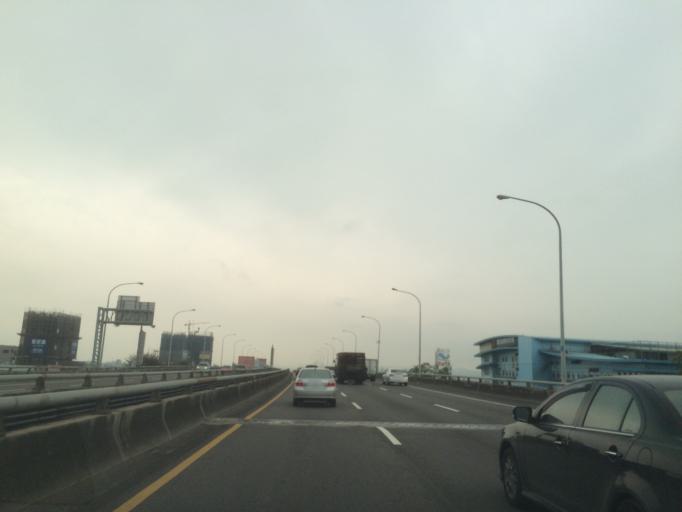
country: TW
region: Taiwan
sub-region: Taichung City
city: Taichung
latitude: 24.1507
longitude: 120.6235
